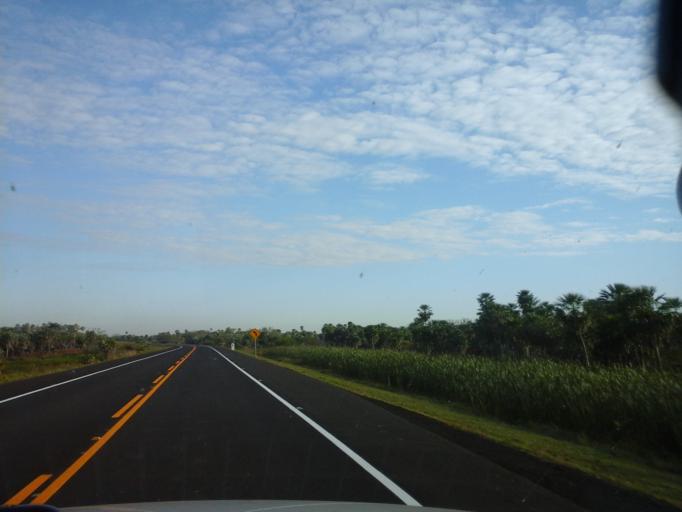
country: PY
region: Neembucu
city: Cerrito
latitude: -26.8710
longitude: -57.7551
